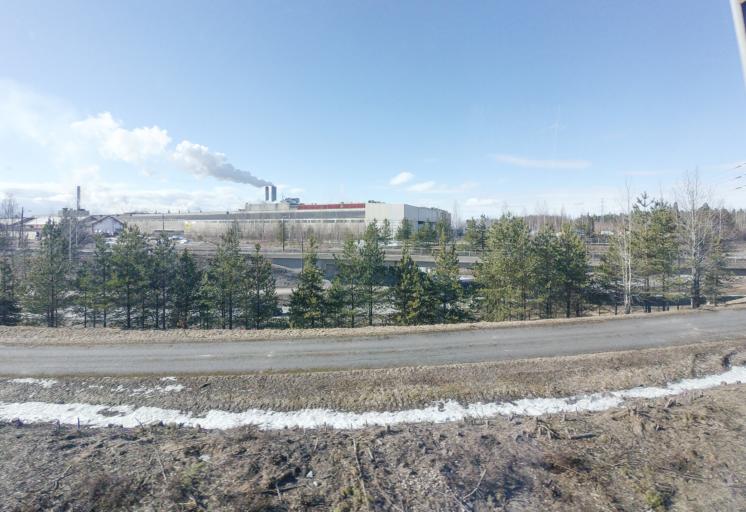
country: FI
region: South Karelia
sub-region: Lappeenranta
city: Lappeenranta
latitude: 61.0629
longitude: 28.2549
